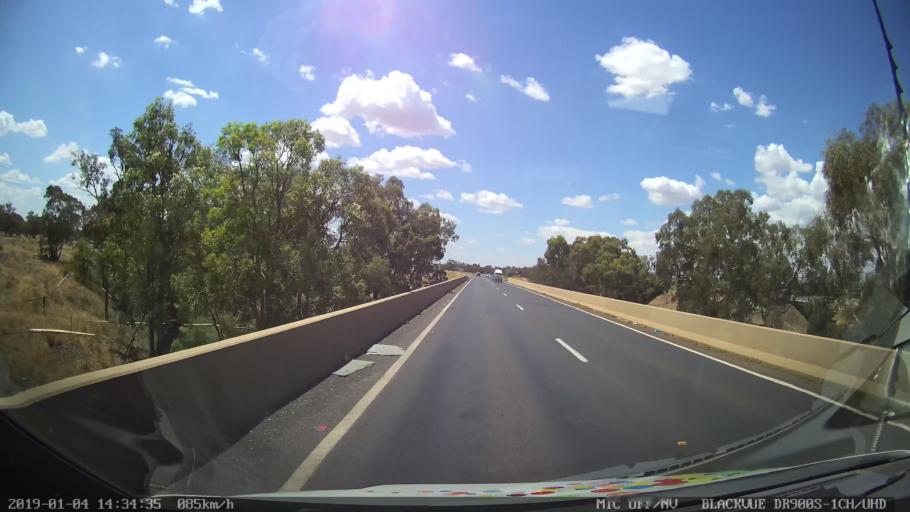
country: AU
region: New South Wales
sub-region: Dubbo Municipality
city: Dubbo
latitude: -32.1966
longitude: 148.6207
